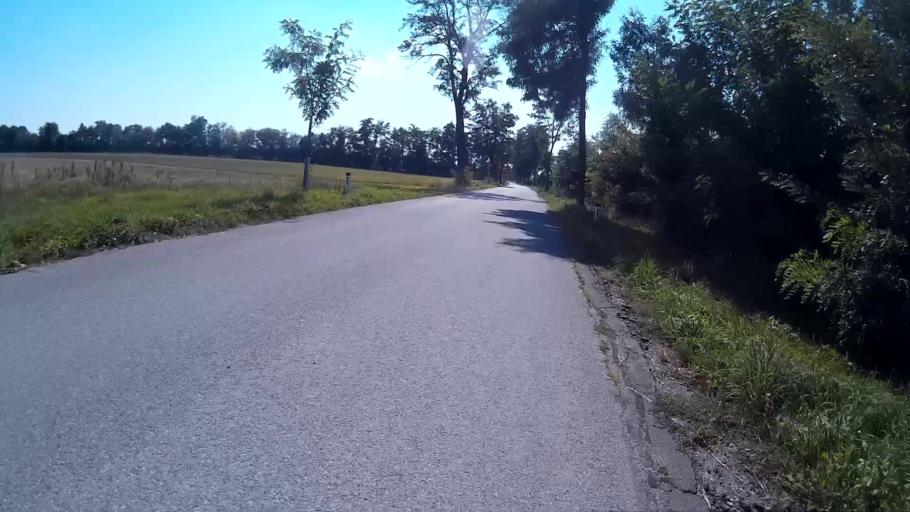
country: CZ
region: South Moravian
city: Novosedly
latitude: 48.7896
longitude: 16.4899
